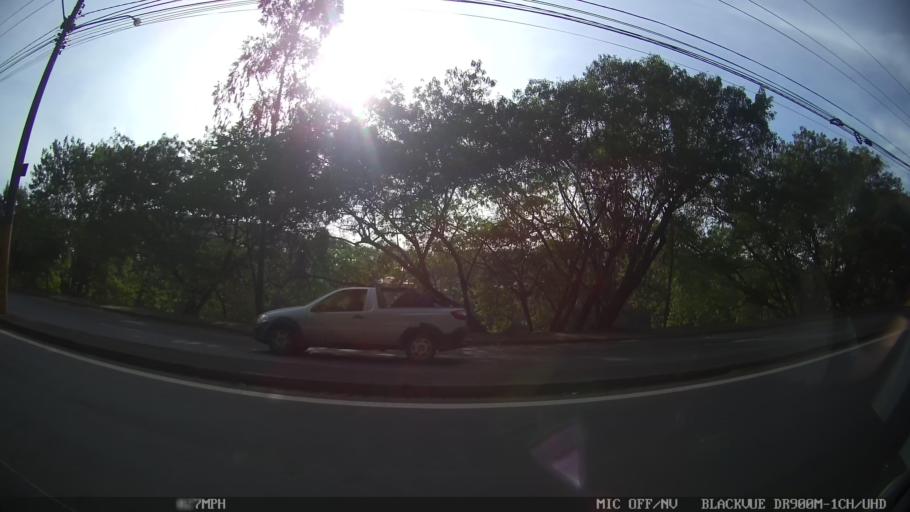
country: BR
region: Sao Paulo
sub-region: Piracicaba
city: Piracicaba
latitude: -22.7225
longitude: -47.6723
